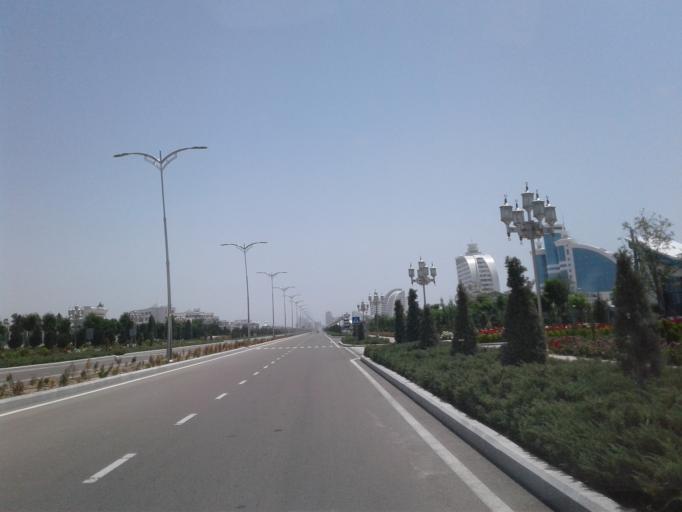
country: TM
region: Balkan
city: Turkmenbasy
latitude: 39.9853
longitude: 52.8250
